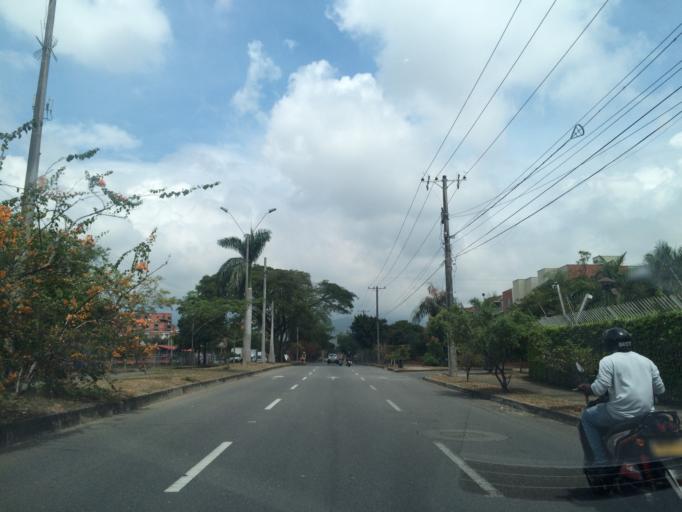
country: CO
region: Valle del Cauca
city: Cali
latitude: 3.3929
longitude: -76.5296
